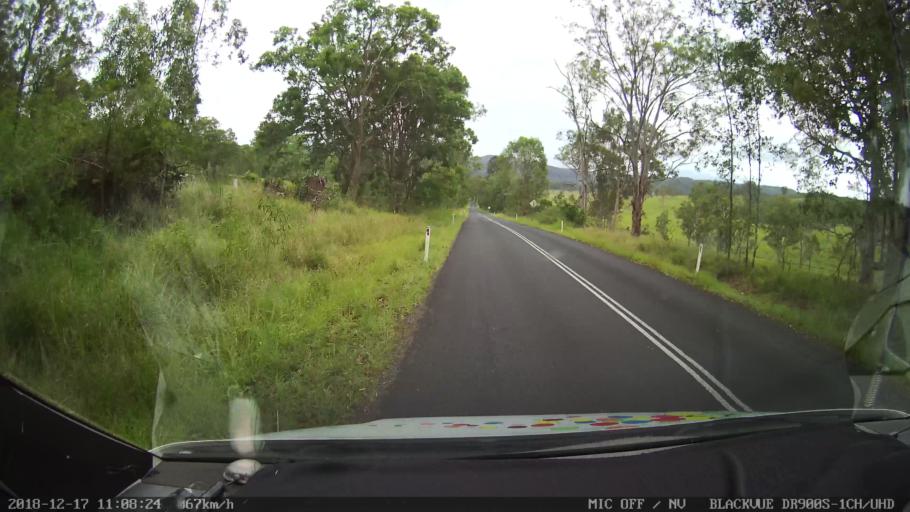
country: AU
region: New South Wales
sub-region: Kyogle
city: Kyogle
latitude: -28.7640
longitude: 152.6544
